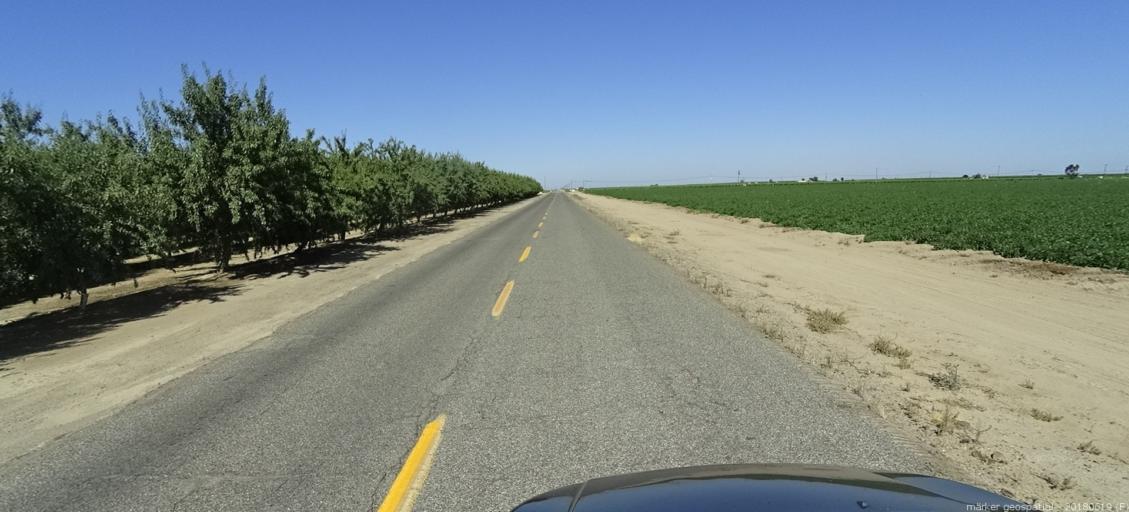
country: US
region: California
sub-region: Fresno County
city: Biola
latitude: 36.8368
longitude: -120.0882
